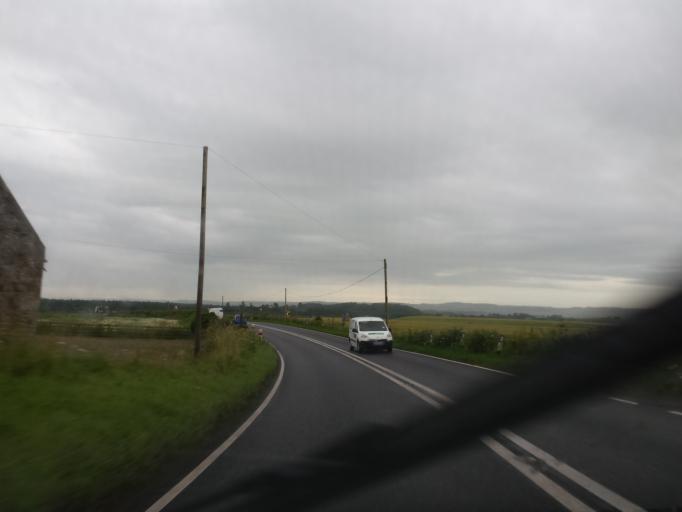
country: GB
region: Scotland
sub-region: Fife
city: Balmullo
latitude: 56.4055
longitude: -2.9153
